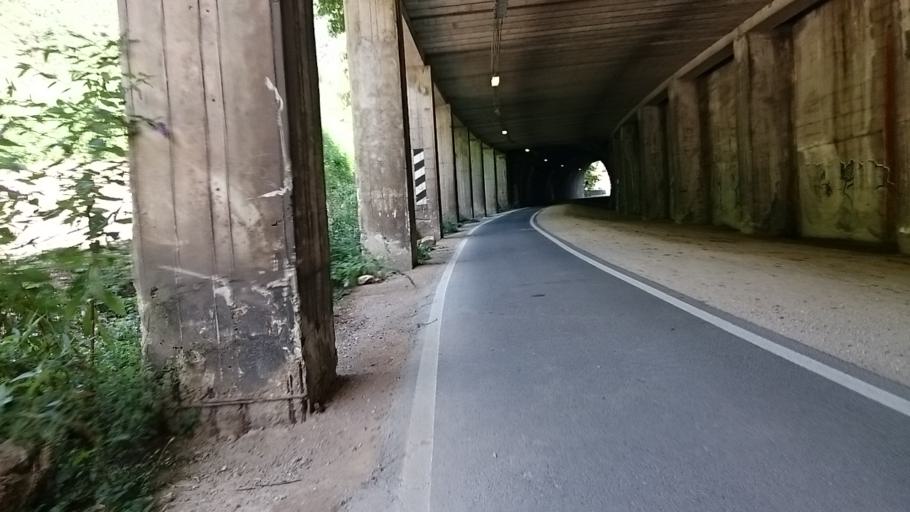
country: IT
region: Trentino-Alto Adige
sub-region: Bolzano
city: Fie Allo Sciliar
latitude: 46.5312
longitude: 11.4889
